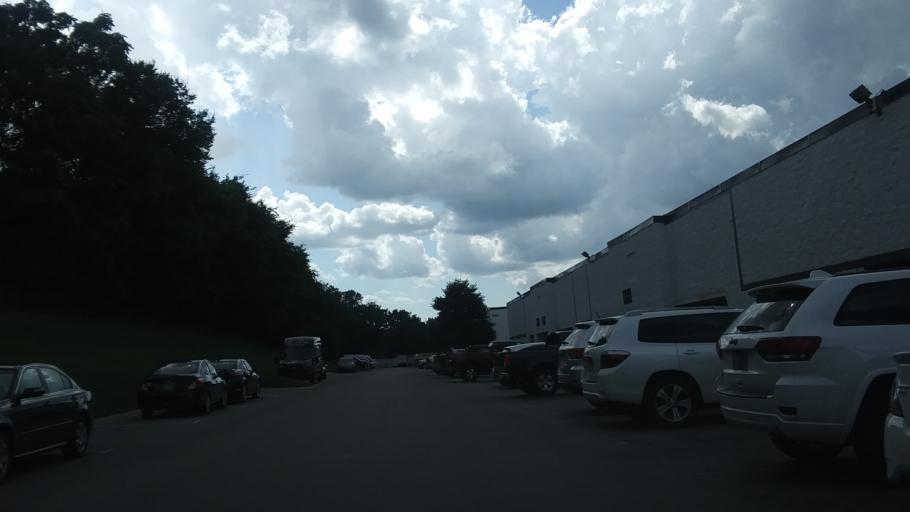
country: US
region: Tennessee
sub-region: Davidson County
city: Oak Hill
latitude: 36.0747
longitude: -86.6958
